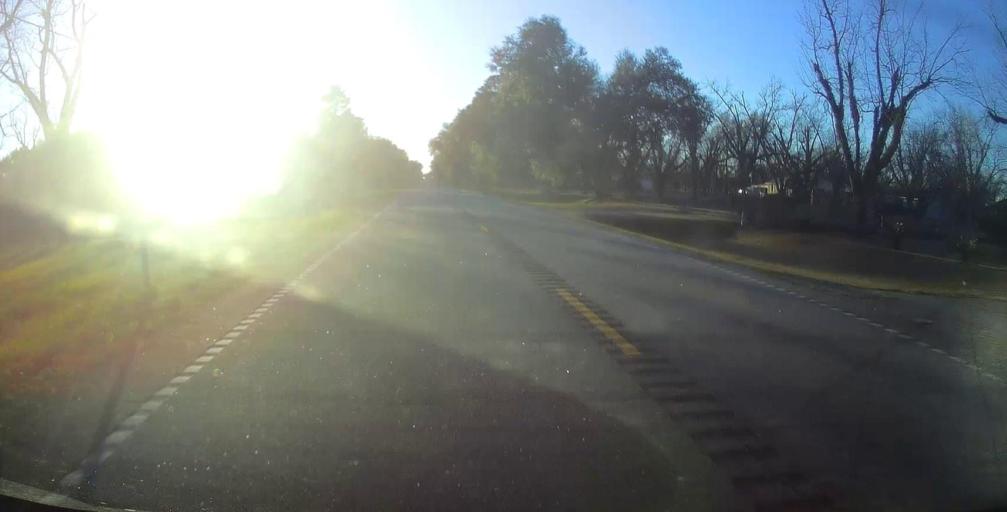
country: US
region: Georgia
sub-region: Dougherty County
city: Albany
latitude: 31.5041
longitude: -84.2303
